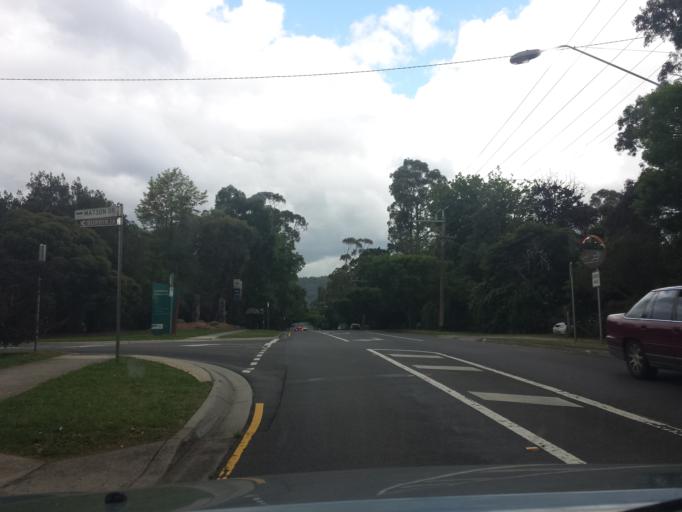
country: AU
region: Victoria
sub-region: Yarra Ranges
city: Belgrave South
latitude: -37.9177
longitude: 145.3343
